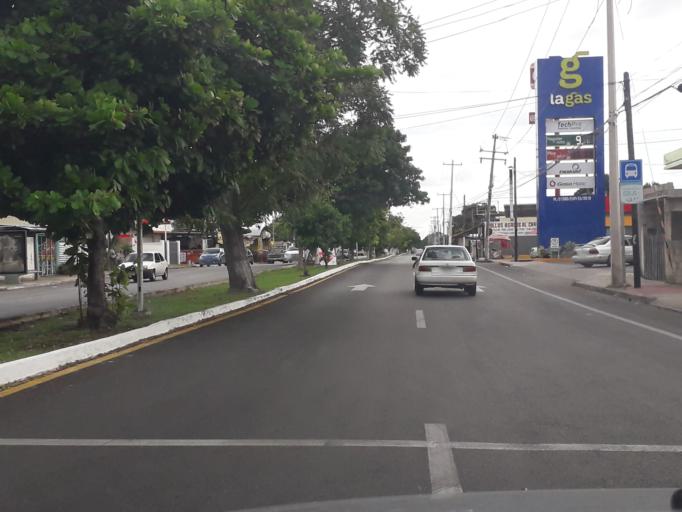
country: MX
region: Yucatan
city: Merida
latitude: 20.9717
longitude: -89.6636
